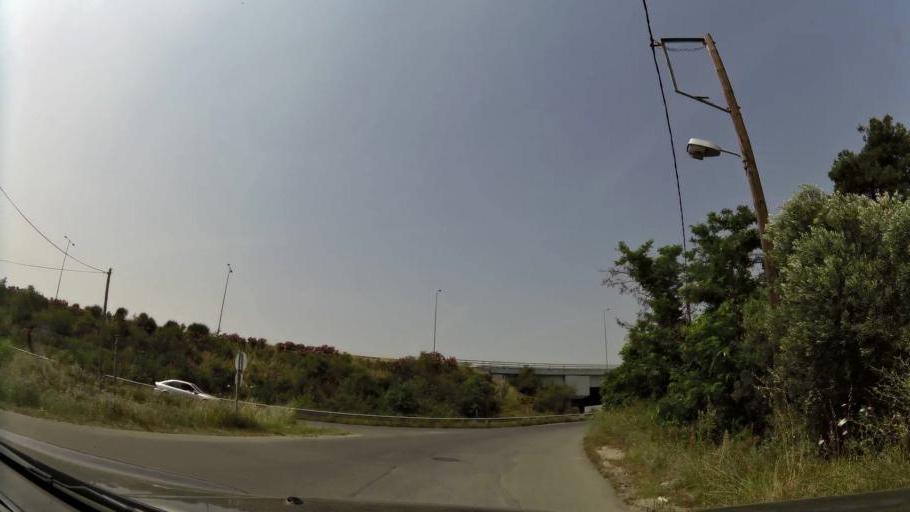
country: GR
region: Central Macedonia
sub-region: Nomos Thessalonikis
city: Nea Magnisia
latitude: 40.6911
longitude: 22.8411
